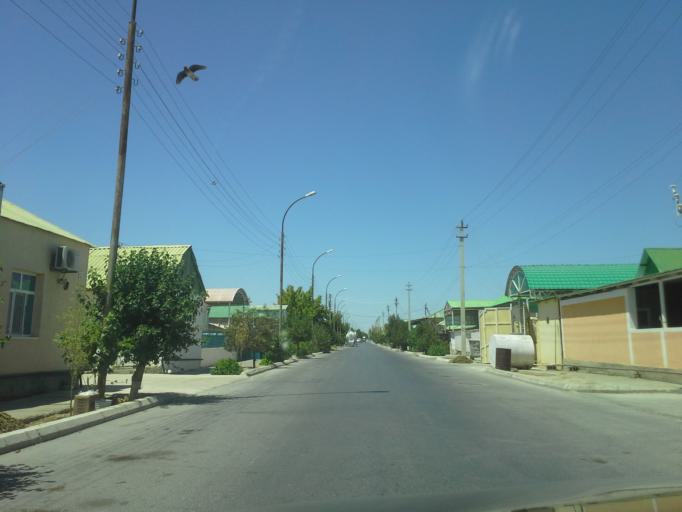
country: TM
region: Ahal
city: Abadan
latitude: 38.0268
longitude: 58.2586
